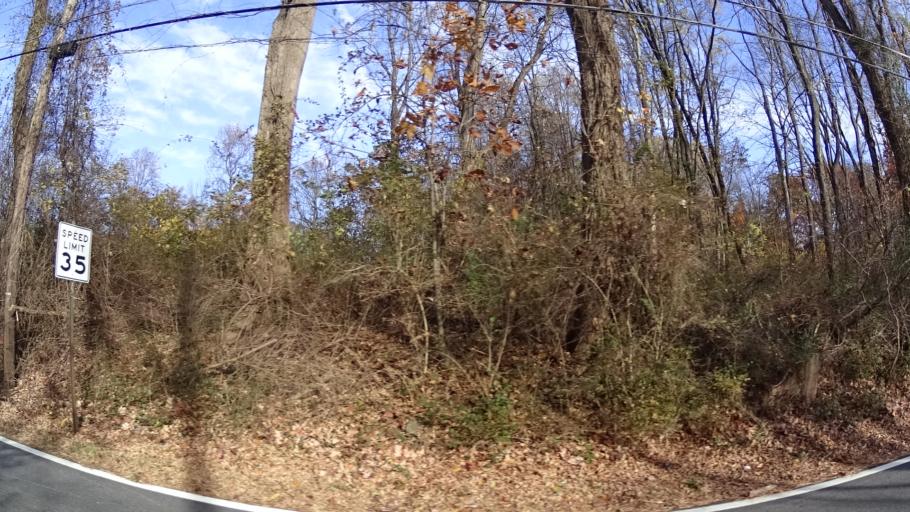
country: US
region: New Jersey
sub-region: Morris County
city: Morristown
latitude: 40.7348
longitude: -74.4987
